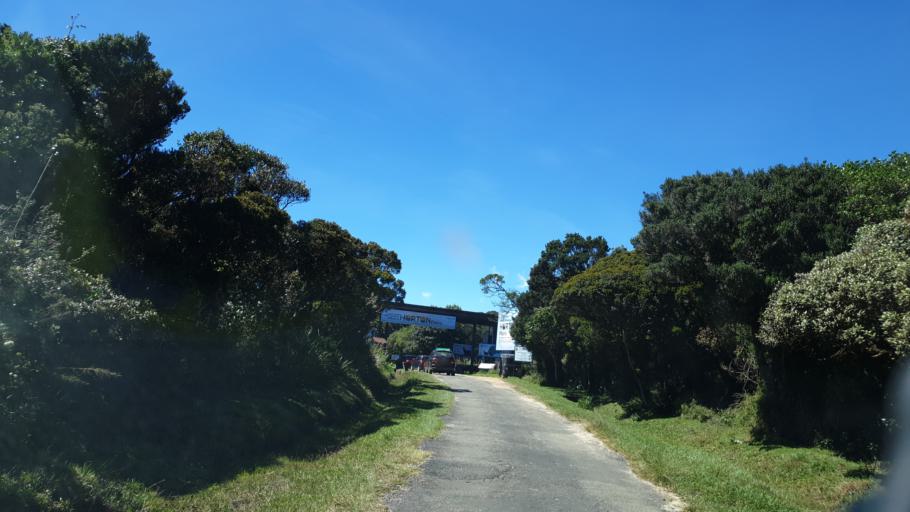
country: LK
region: Uva
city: Haputale
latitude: 6.8077
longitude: 80.8355
